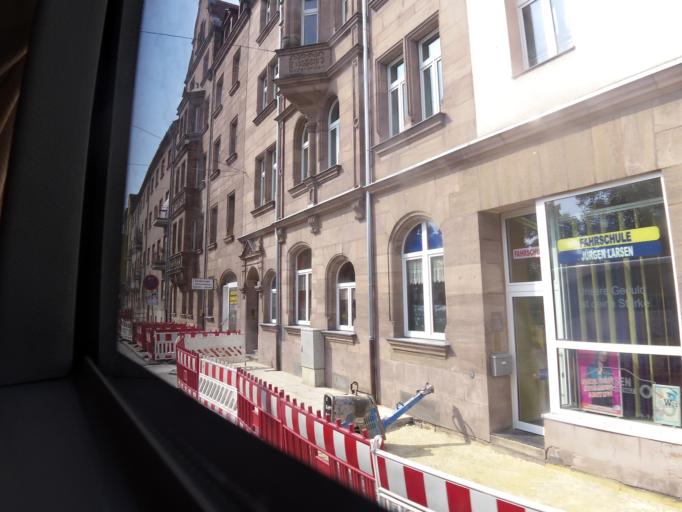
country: DE
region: Bavaria
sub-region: Regierungsbezirk Mittelfranken
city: Nuernberg
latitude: 49.4426
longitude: 11.1000
